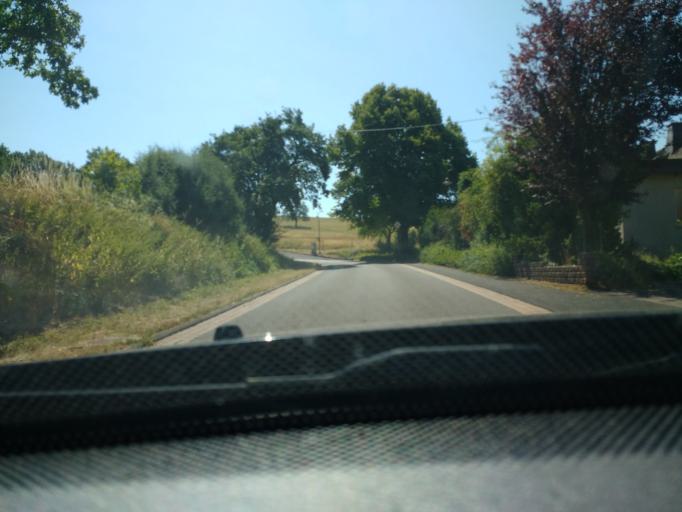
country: DE
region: Rheinland-Pfalz
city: Flussbach
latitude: 50.0162
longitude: 6.9302
